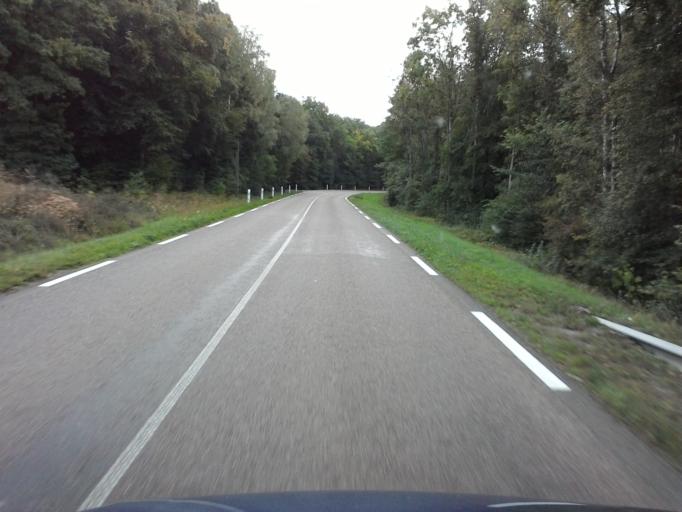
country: FR
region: Lorraine
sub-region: Departement des Vosges
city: Neufchateau
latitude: 48.3447
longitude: 5.6573
